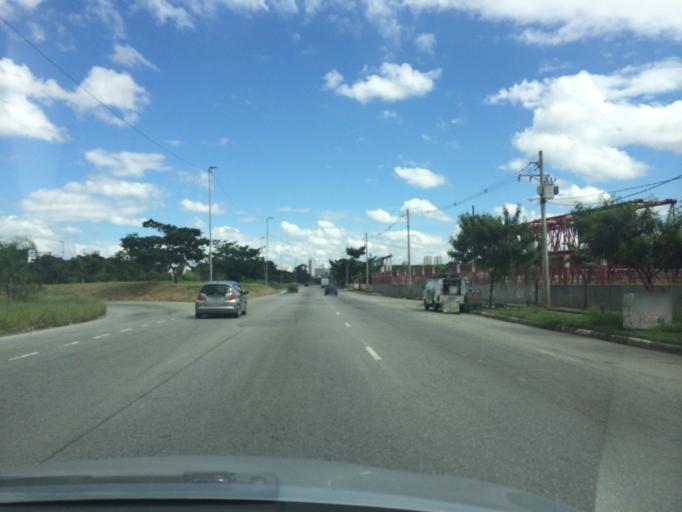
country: BR
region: Sao Paulo
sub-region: Guarulhos
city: Guarulhos
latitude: -23.5093
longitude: -46.5592
